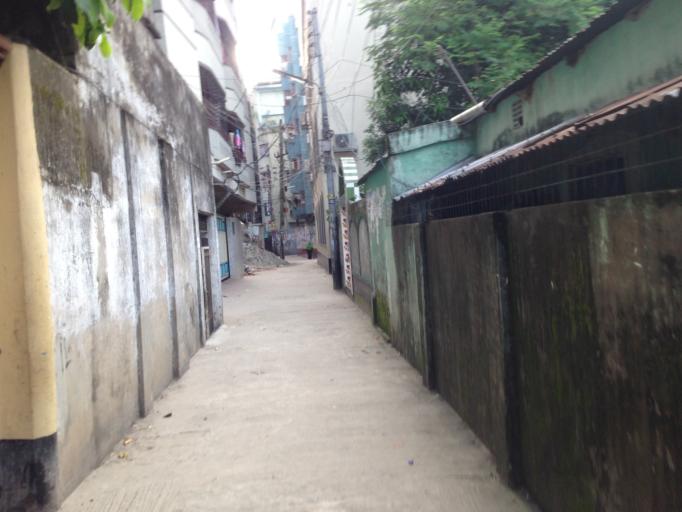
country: BD
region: Dhaka
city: Azimpur
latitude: 23.8039
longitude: 90.3720
